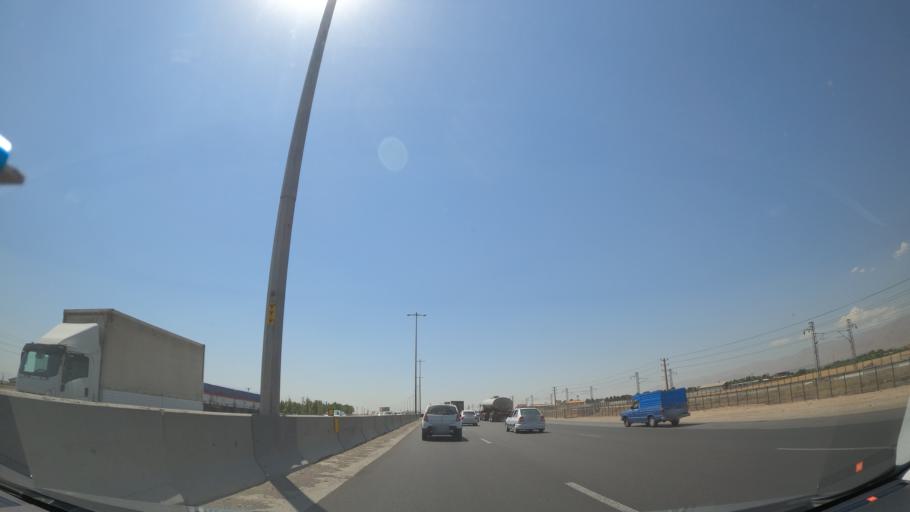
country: IR
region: Alborz
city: Hashtgerd
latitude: 35.9118
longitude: 50.8293
